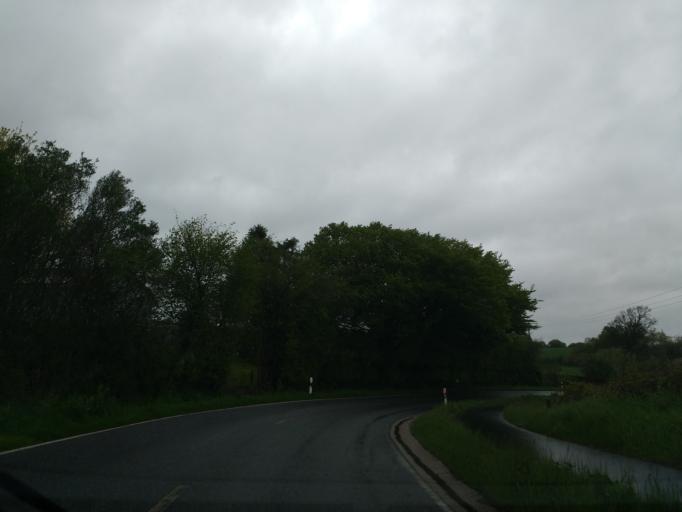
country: DE
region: Schleswig-Holstein
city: Waabs
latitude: 54.5276
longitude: 9.9677
